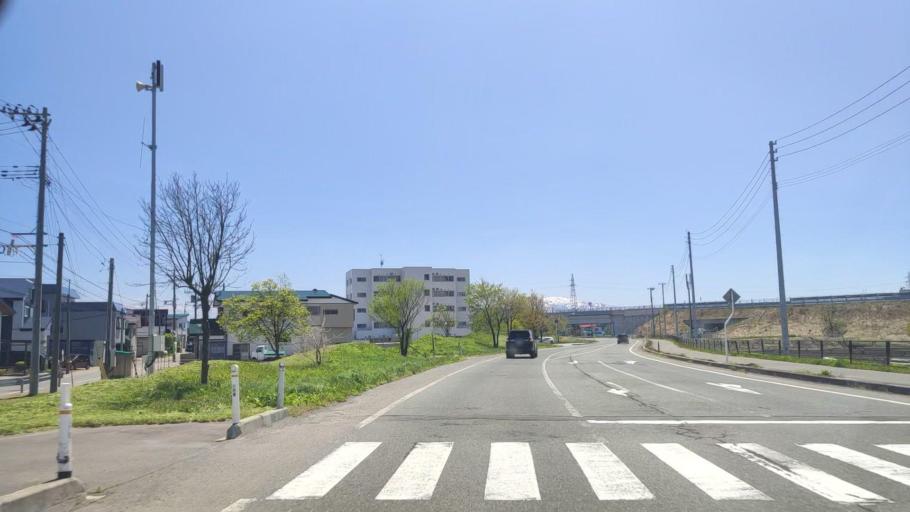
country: JP
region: Yamagata
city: Shinjo
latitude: 38.7469
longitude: 140.2956
